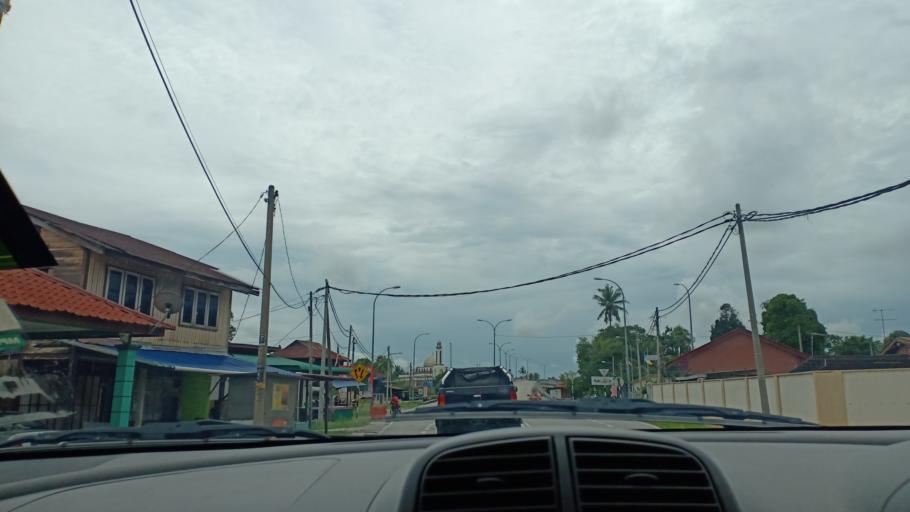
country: MY
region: Penang
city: Bukit Mertajam
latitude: 5.4077
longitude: 100.4760
